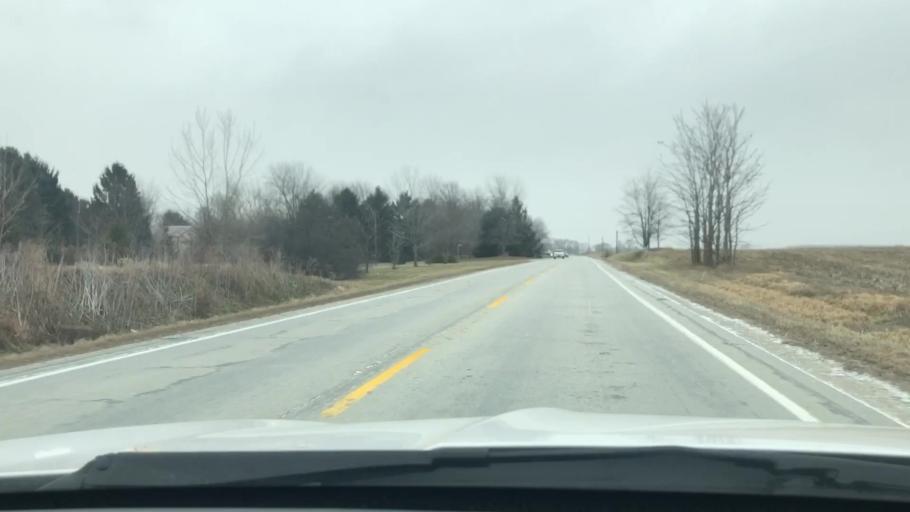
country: US
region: Indiana
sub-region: Fulton County
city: Akron
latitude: 41.0392
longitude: -86.0777
